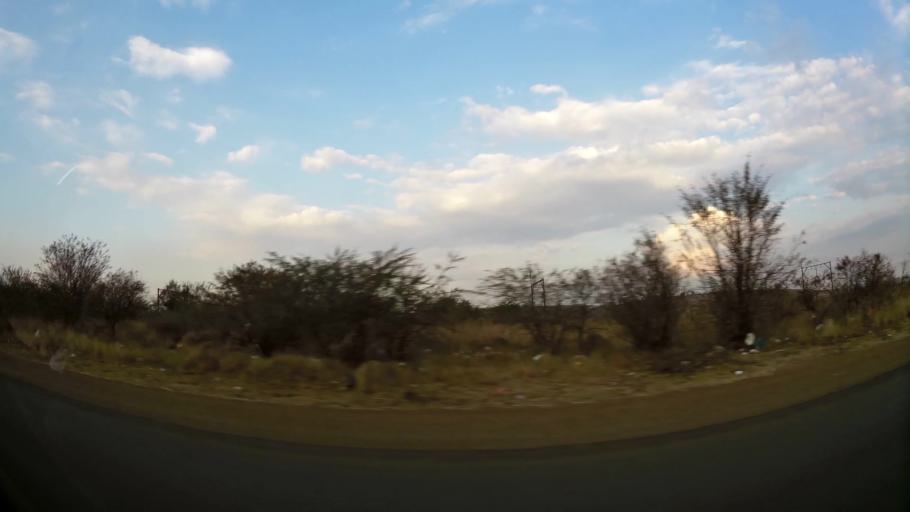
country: ZA
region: Gauteng
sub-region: City of Johannesburg Metropolitan Municipality
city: Orange Farm
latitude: -26.5857
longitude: 27.8542
